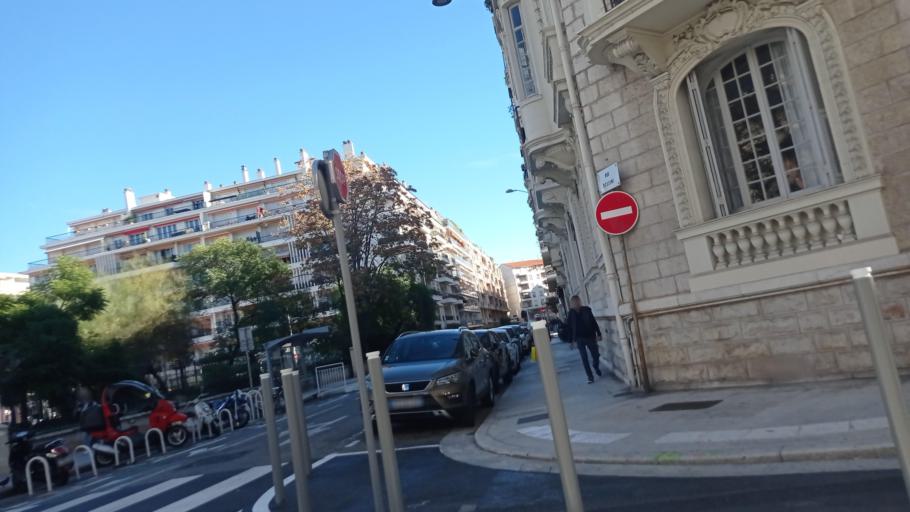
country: FR
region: Provence-Alpes-Cote d'Azur
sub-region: Departement des Alpes-Maritimes
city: Nice
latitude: 43.7004
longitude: 7.2614
